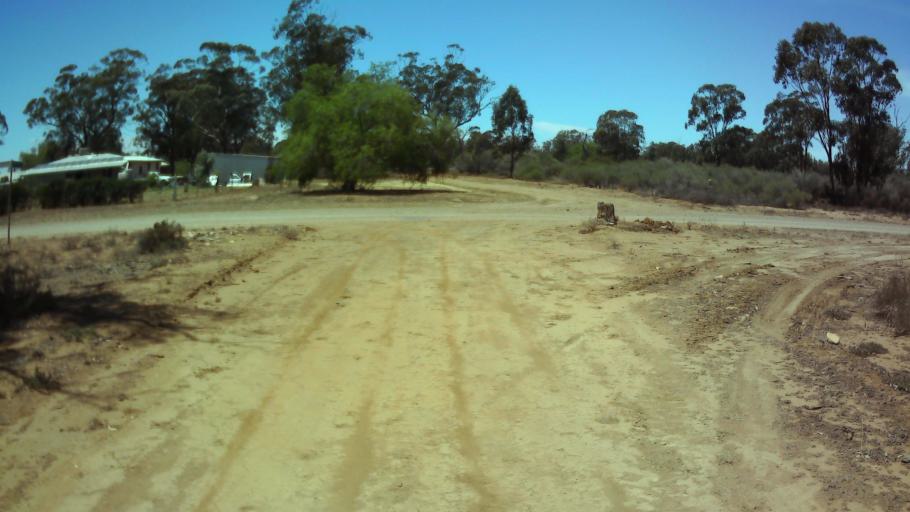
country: AU
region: New South Wales
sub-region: Weddin
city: Grenfell
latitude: -33.8450
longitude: 147.7386
